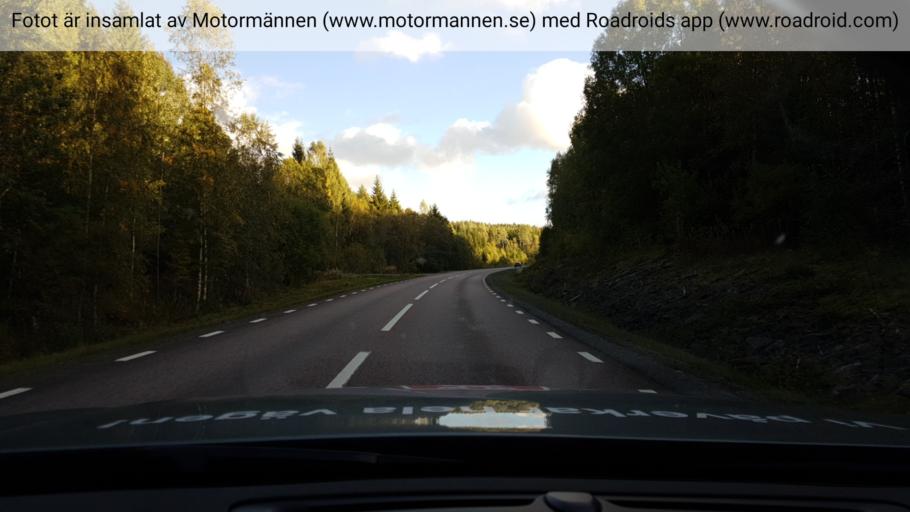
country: SE
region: Vaermland
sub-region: Karlstads Kommun
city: Molkom
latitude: 59.6597
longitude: 13.7086
